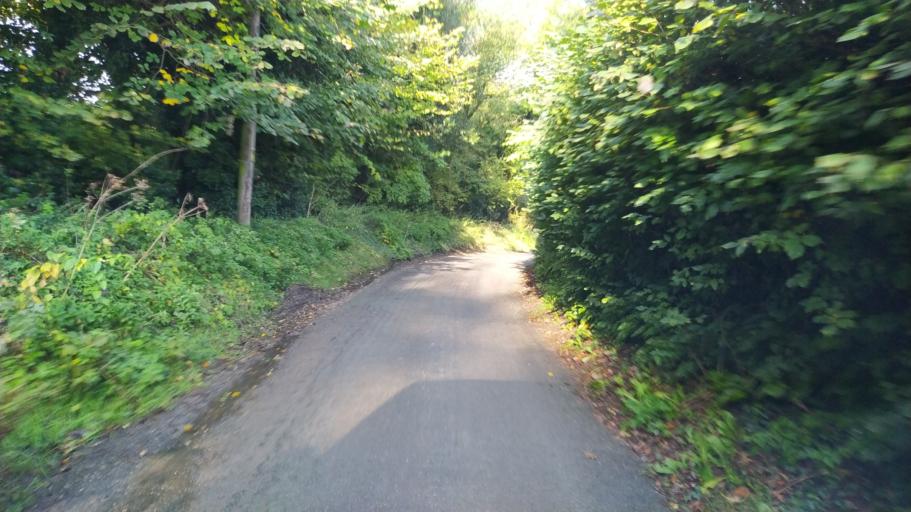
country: GB
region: England
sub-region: Wiltshire
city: Hindon
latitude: 51.0314
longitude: -2.1346
